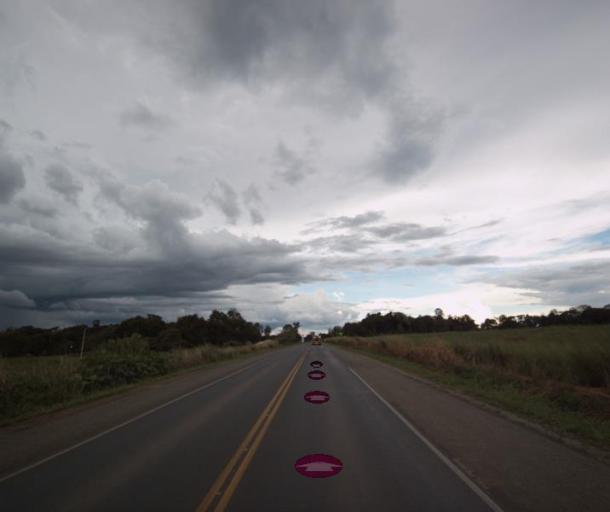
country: BR
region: Goias
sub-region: Itapaci
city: Itapaci
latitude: -15.0268
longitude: -49.4293
